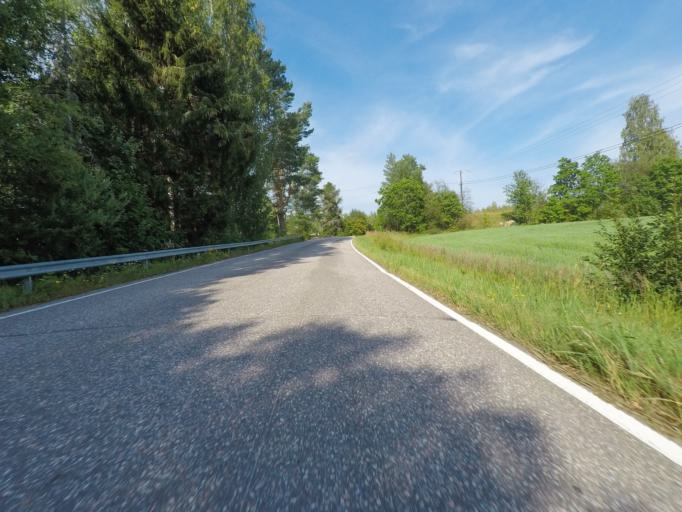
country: FI
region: Southern Savonia
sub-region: Savonlinna
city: Sulkava
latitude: 61.7611
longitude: 28.2328
